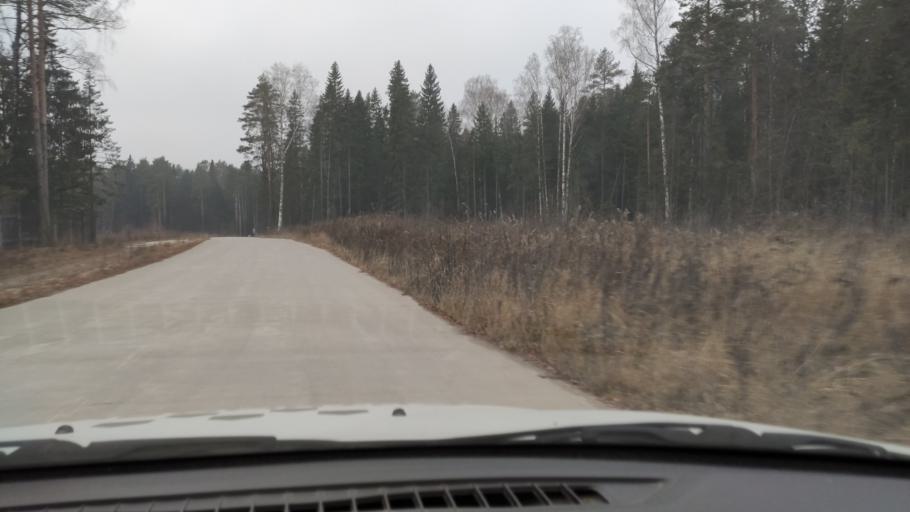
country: RU
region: Perm
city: Kondratovo
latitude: 58.0473
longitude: 56.1429
